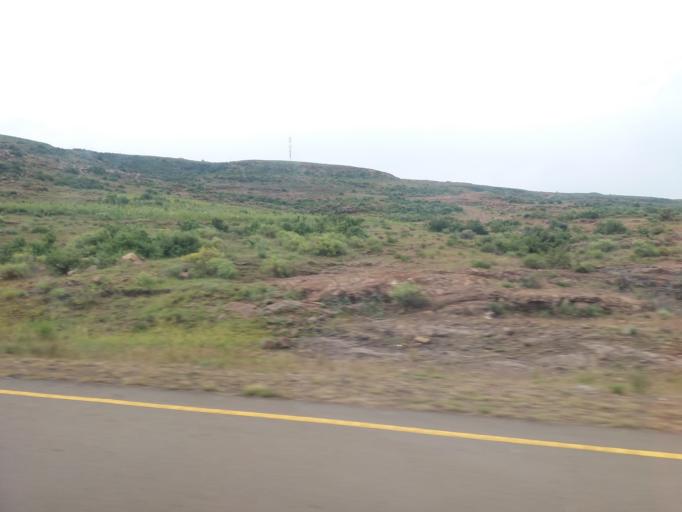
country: LS
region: Berea
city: Teyateyaneng
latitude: -29.3239
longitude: 27.7615
